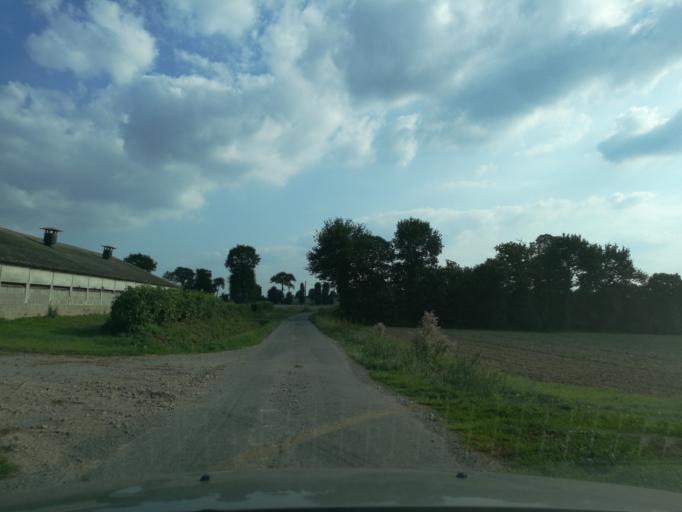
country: FR
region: Brittany
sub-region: Departement d'Ille-et-Vilaine
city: Montauban-de-Bretagne
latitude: 48.1989
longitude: -1.9949
